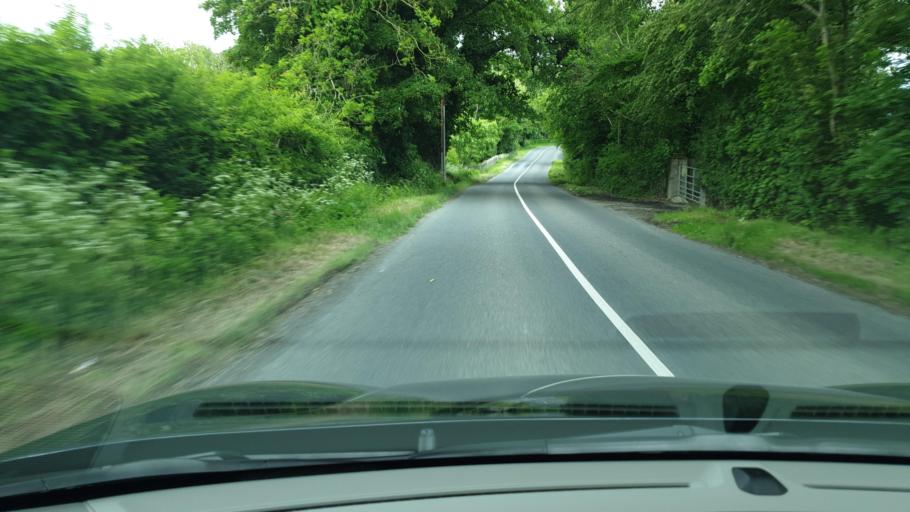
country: IE
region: Leinster
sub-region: An Mhi
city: Slane
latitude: 53.7779
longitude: -6.6321
